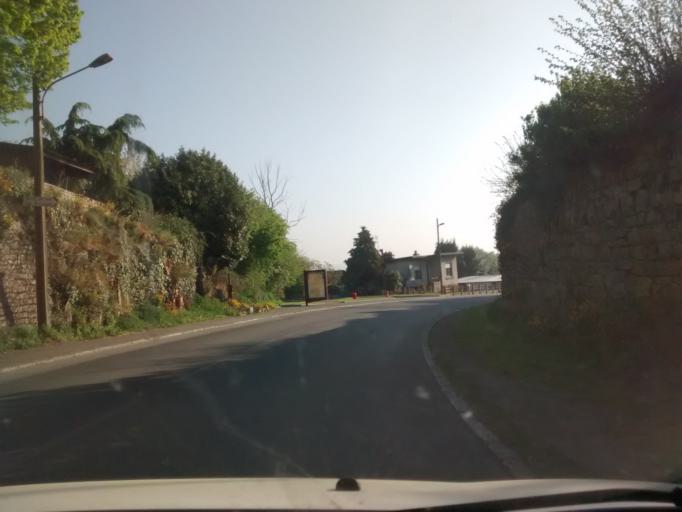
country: FR
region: Brittany
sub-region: Departement d'Ille-et-Vilaine
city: Saint-Aubin-du-Cormier
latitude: 48.2616
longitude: -1.4040
